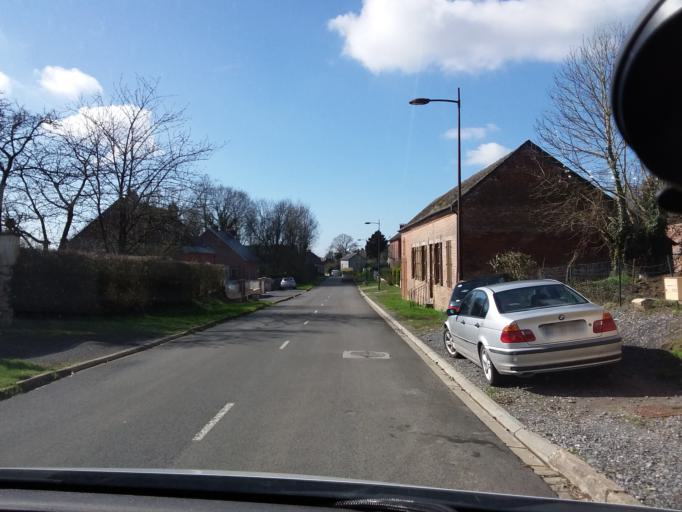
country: FR
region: Picardie
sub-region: Departement de l'Aisne
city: Origny-en-Thierache
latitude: 49.8064
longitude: 4.0142
